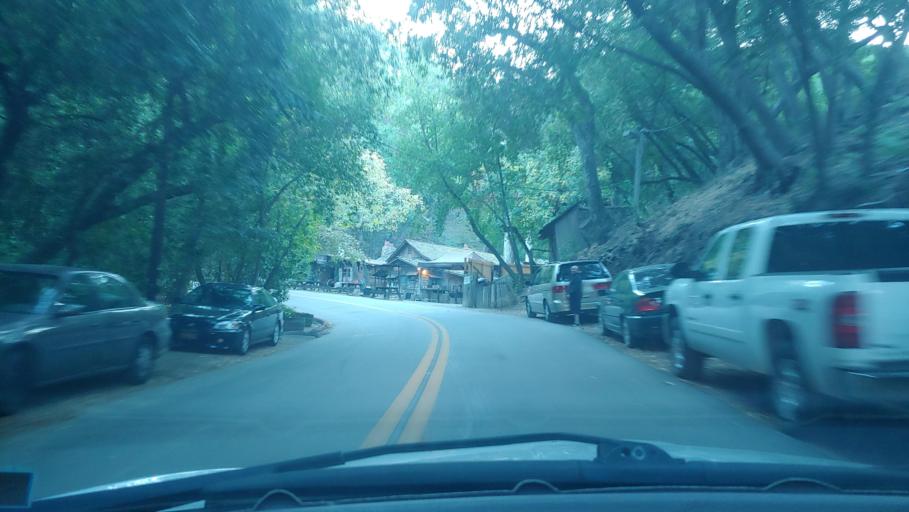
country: US
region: California
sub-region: Santa Barbara County
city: Goleta
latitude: 34.5221
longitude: -119.8399
